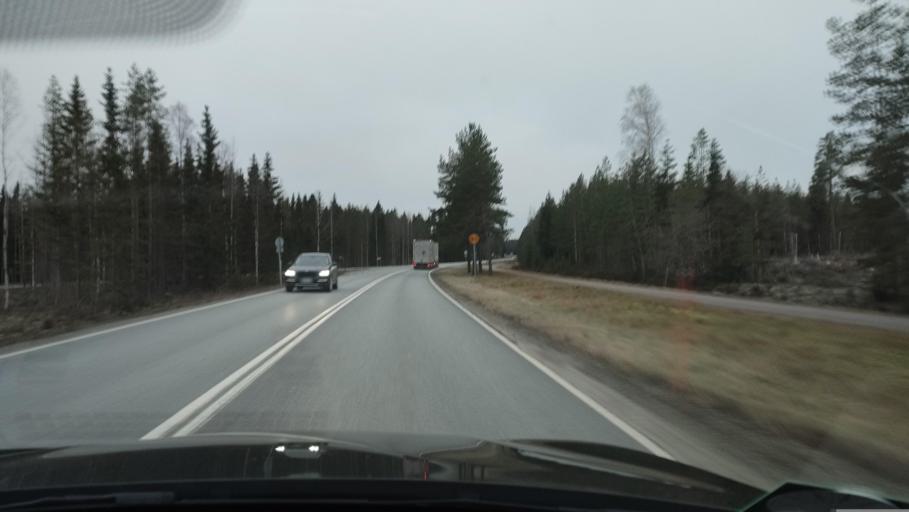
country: FI
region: Southern Ostrobothnia
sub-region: Suupohja
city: Kauhajoki
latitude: 62.3945
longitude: 22.1551
